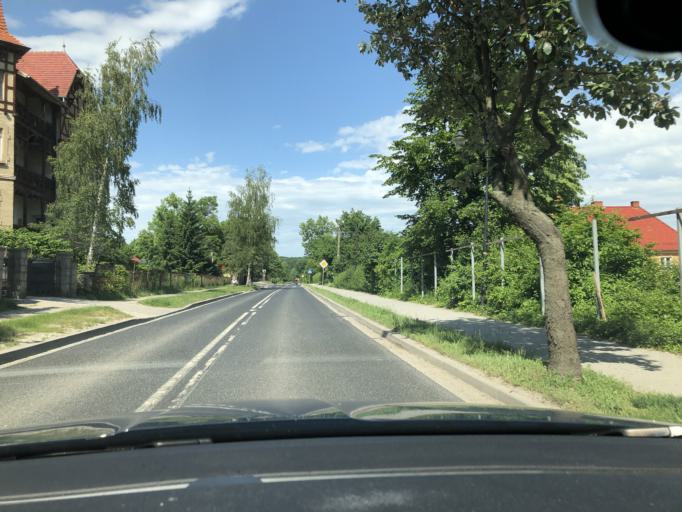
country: PL
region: Lower Silesian Voivodeship
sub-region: Powiat jaworski
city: Bolkow
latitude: 50.9283
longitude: 16.1065
